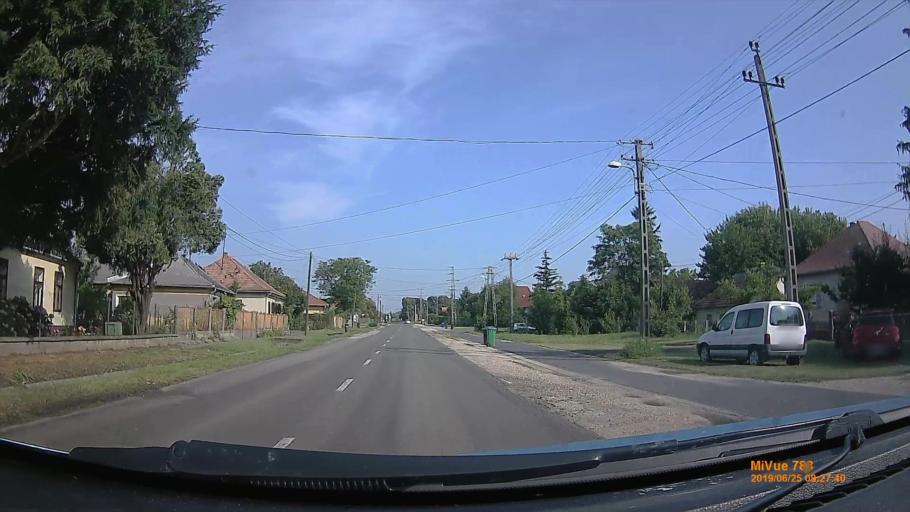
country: HU
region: Fejer
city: Szabadbattyan
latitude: 47.1143
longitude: 18.3791
